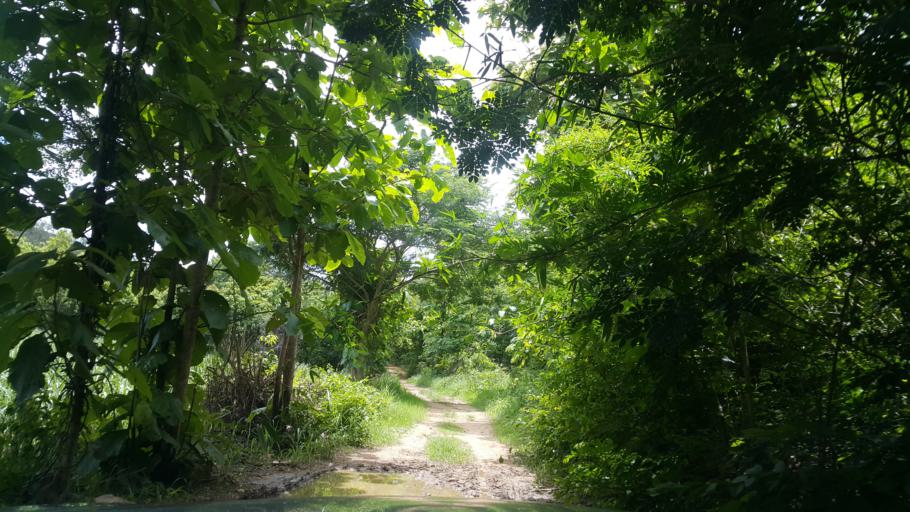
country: TH
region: Sukhothai
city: Thung Saliam
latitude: 17.3312
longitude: 99.4738
